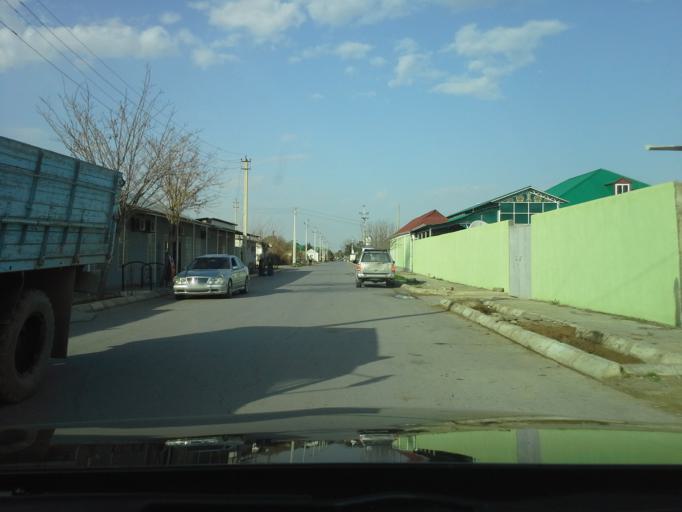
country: TM
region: Ahal
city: Abadan
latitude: 38.0223
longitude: 58.2330
